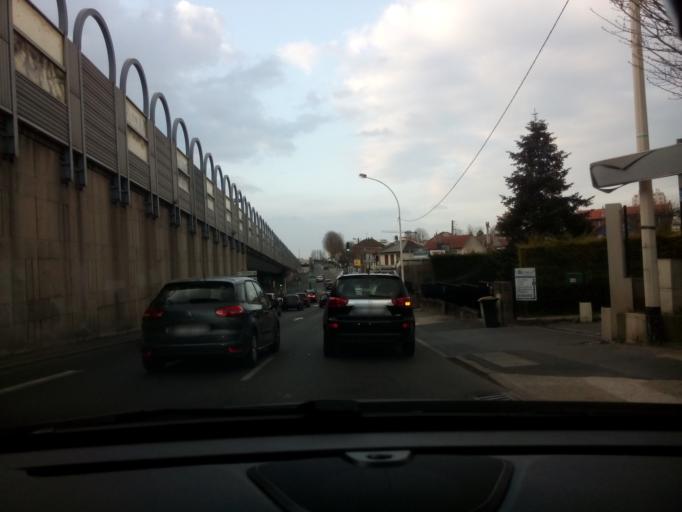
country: FR
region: Ile-de-France
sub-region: Departement du Val-de-Marne
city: Cachan
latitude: 48.7985
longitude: 2.3441
